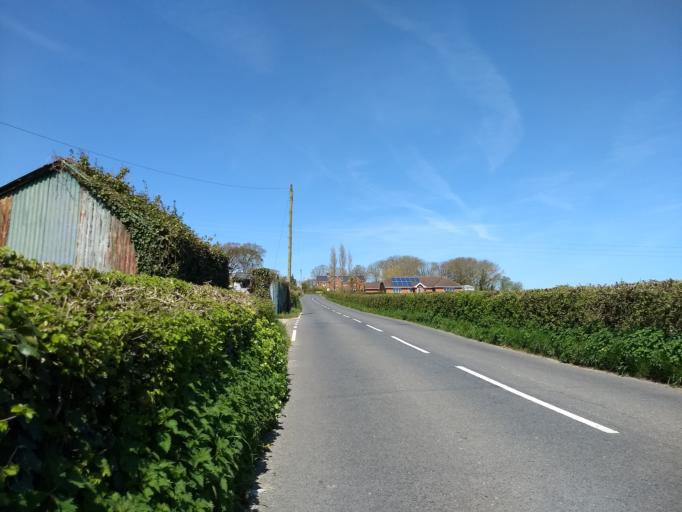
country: GB
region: England
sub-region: Isle of Wight
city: Northwood
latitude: 50.7392
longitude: -1.3345
